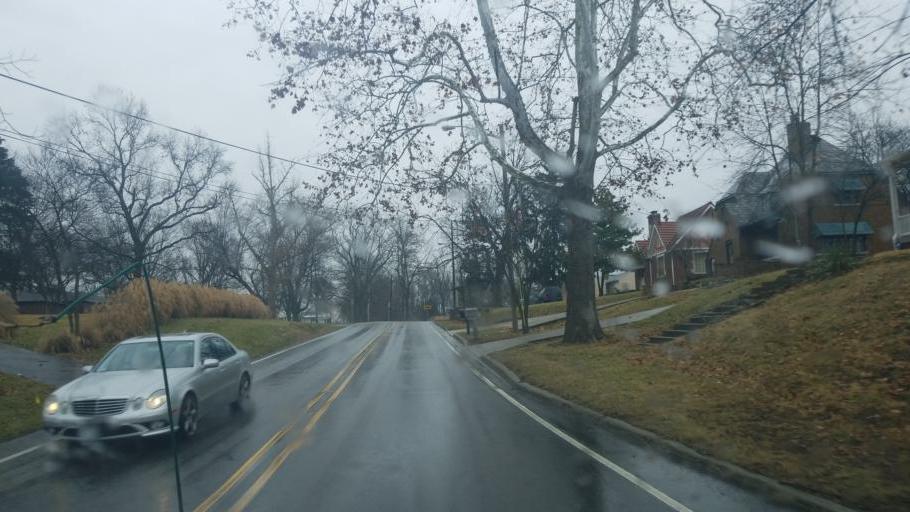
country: US
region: Indiana
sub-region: Shelby County
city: Shelbyville
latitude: 39.5099
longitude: -85.7727
